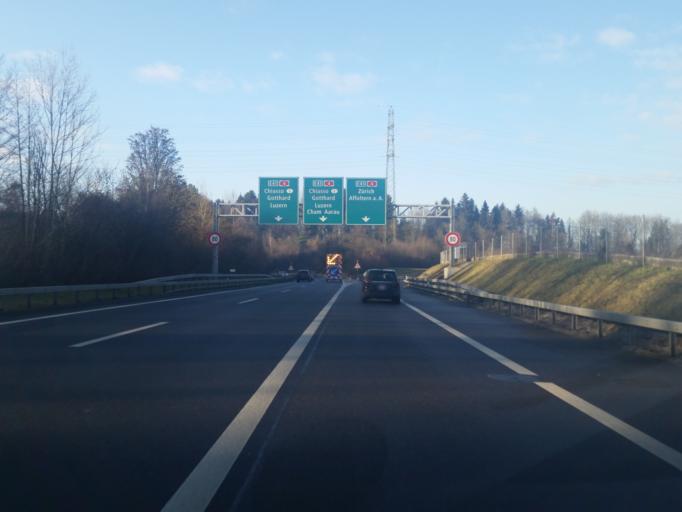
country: CH
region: Zug
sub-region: Zug
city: Cham
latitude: 47.1989
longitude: 8.4637
